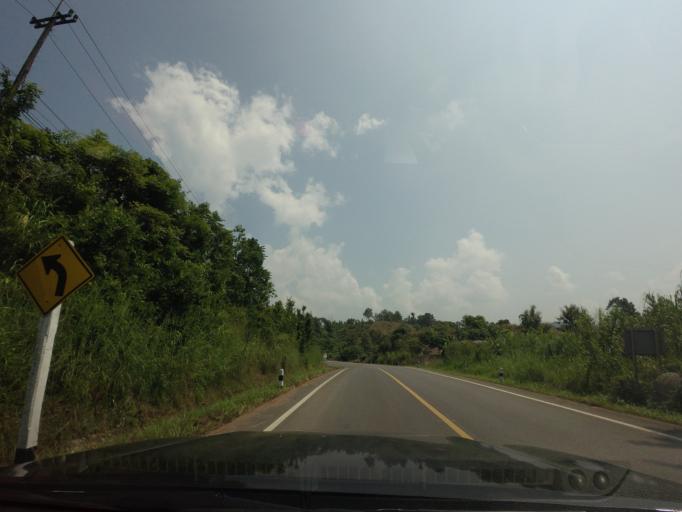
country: TH
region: Nan
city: Santi Suk
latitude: 18.8933
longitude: 100.8379
